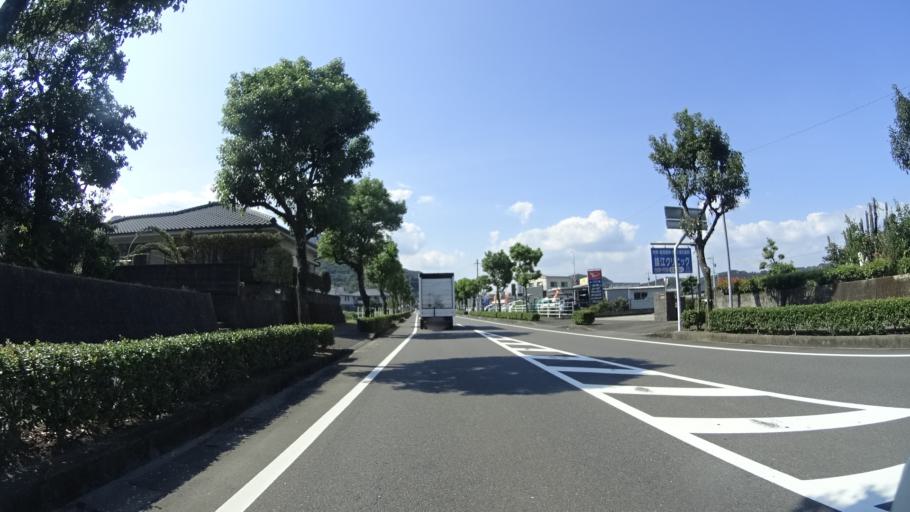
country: JP
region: Kagoshima
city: Kajiki
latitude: 31.7090
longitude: 130.6051
